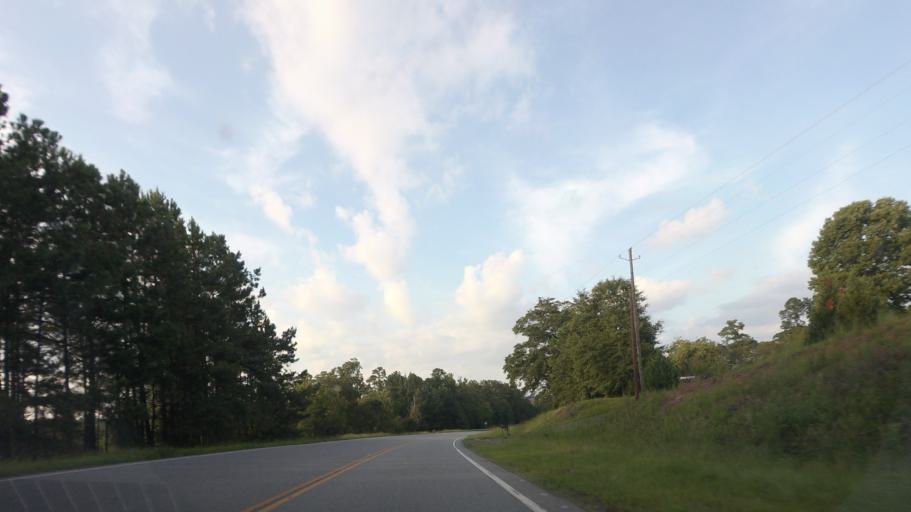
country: US
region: Georgia
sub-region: Wilkinson County
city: Gordon
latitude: 32.8629
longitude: -83.3470
